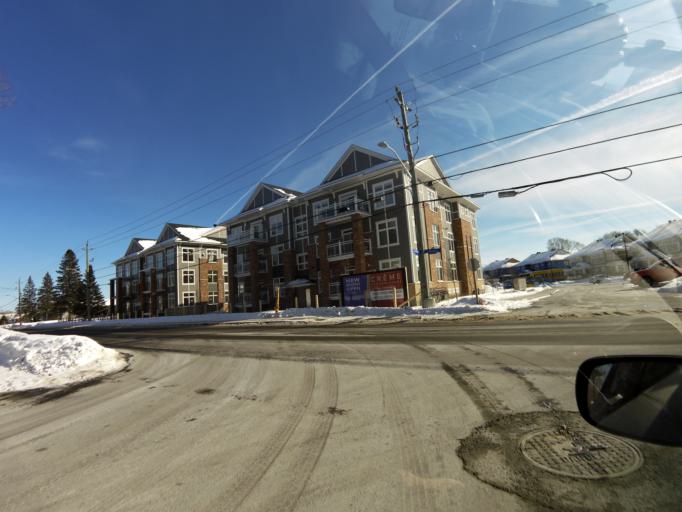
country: CA
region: Ontario
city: Ottawa
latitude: 45.4312
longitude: -75.5140
